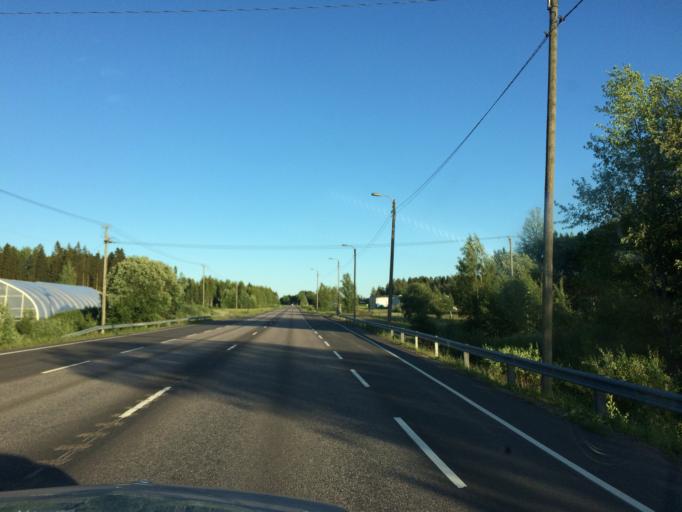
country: FI
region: Haeme
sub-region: Haemeenlinna
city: Tervakoski
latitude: 60.8144
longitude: 24.6439
